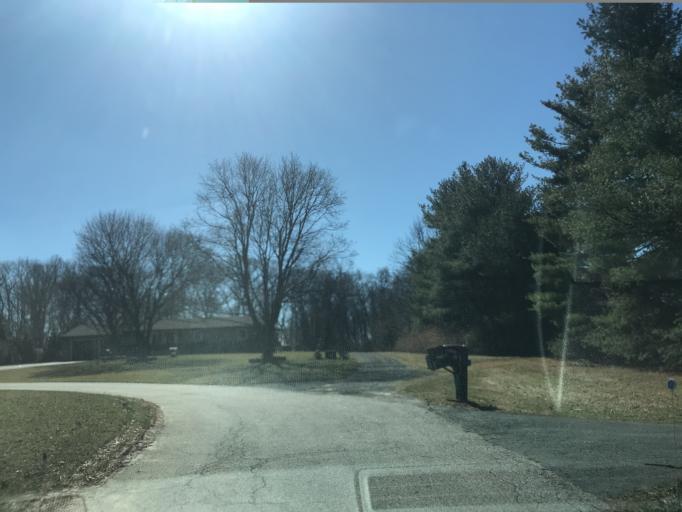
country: US
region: Pennsylvania
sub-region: York County
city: Stewartstown
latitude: 39.7050
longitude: -76.5299
